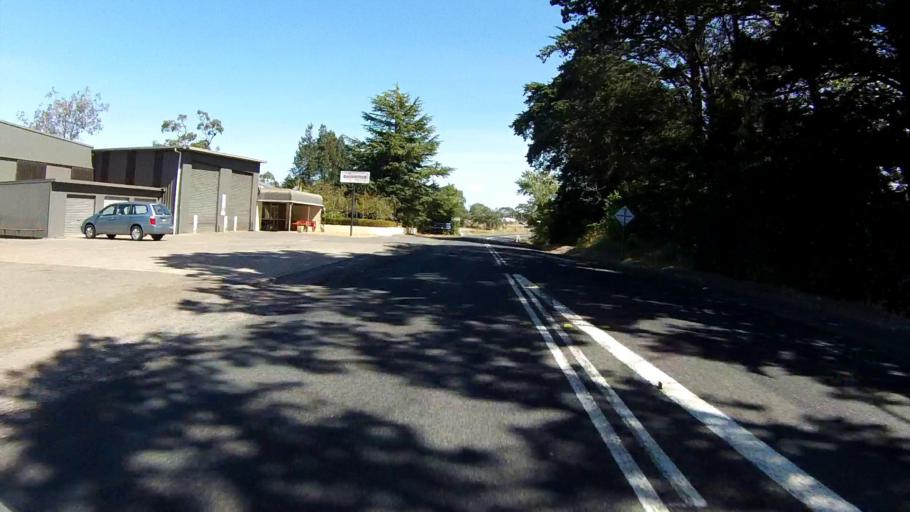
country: AU
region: Tasmania
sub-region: Sorell
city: Sorell
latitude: -42.4988
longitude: 147.9215
